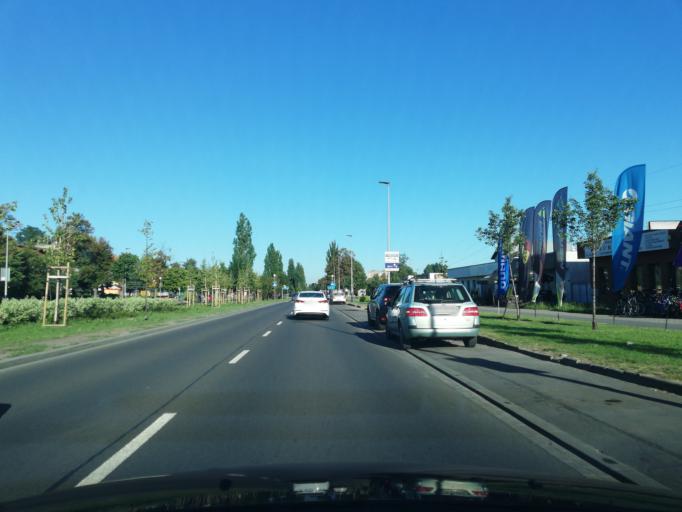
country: PL
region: Lesser Poland Voivodeship
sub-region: Krakow
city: Krakow
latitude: 50.0864
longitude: 20.0101
